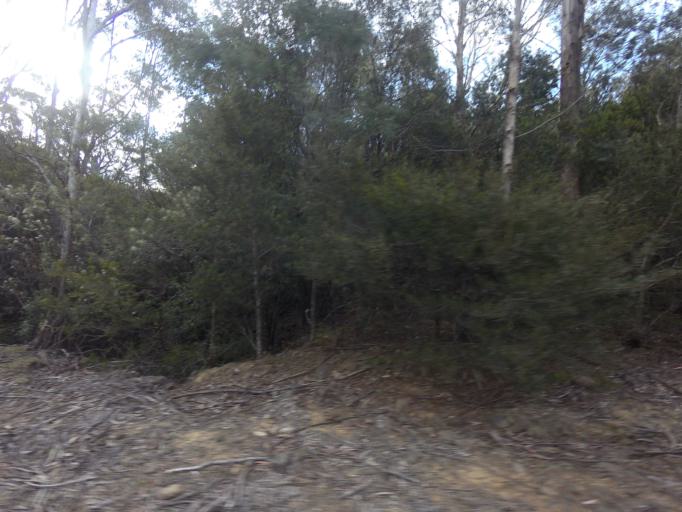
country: AU
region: Tasmania
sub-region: Break O'Day
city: St Helens
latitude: -41.8542
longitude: 148.0396
